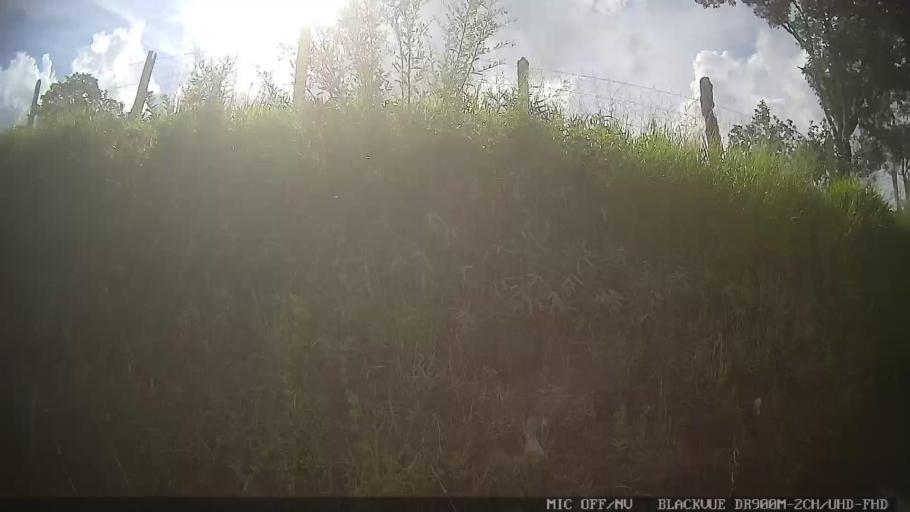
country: BR
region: Minas Gerais
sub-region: Extrema
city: Extrema
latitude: -22.8320
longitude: -46.2471
